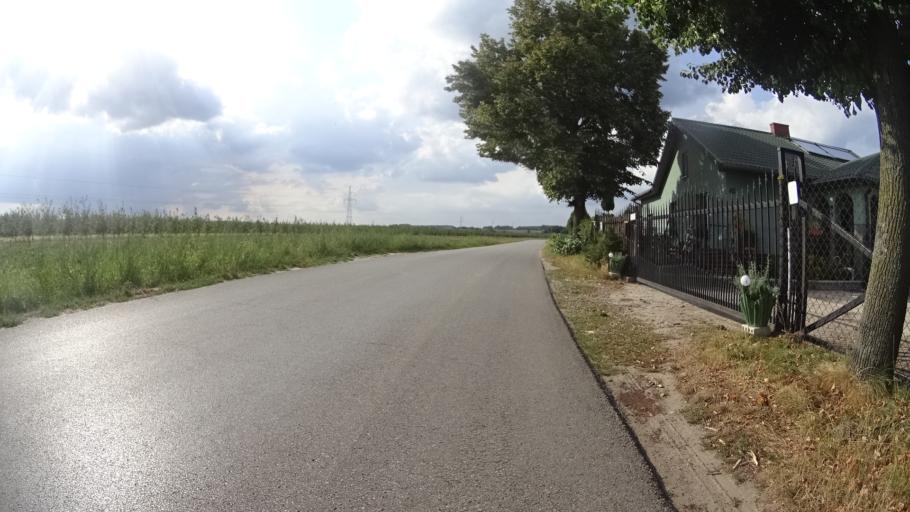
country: PL
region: Masovian Voivodeship
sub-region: Powiat grojecki
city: Mogielnica
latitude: 51.6602
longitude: 20.7475
